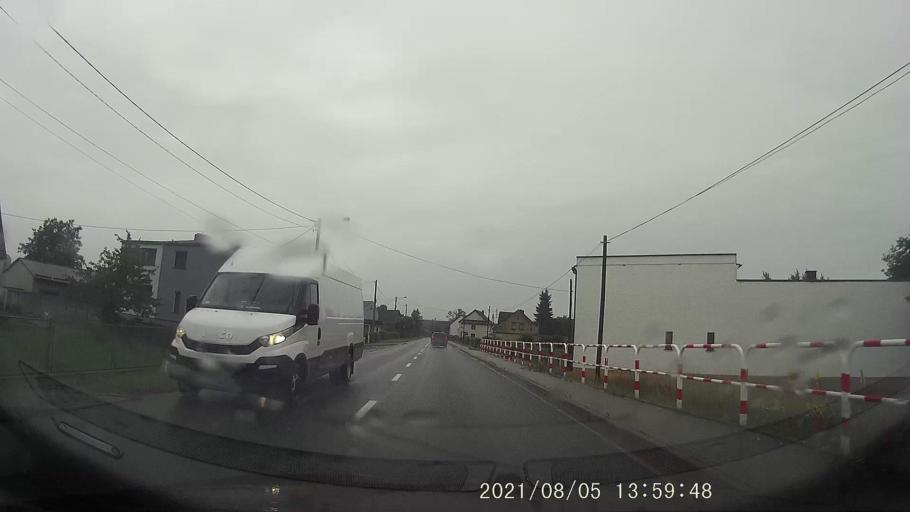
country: PL
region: Opole Voivodeship
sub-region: Powiat krapkowicki
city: Strzeleczki
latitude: 50.4519
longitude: 17.9074
